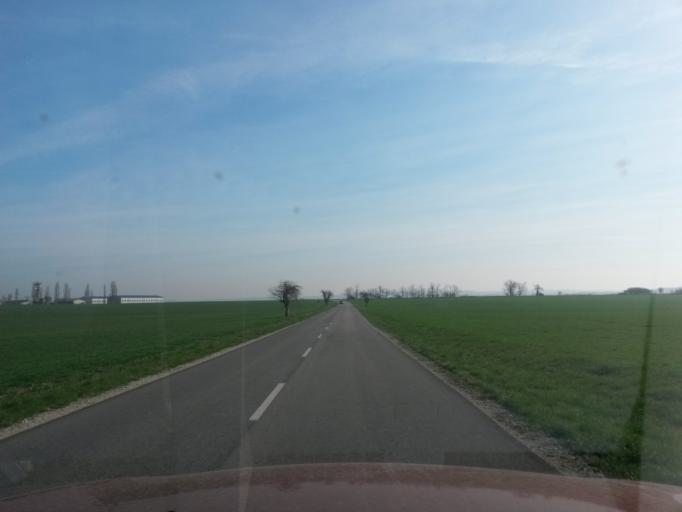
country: SK
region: Nitriansky
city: Svodin
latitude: 47.9773
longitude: 18.3822
